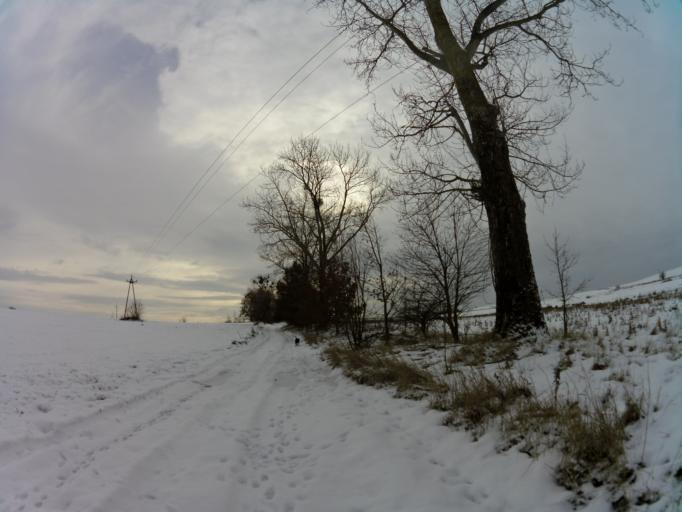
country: PL
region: West Pomeranian Voivodeship
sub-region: Powiat choszczenski
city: Recz
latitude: 53.2894
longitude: 15.5041
